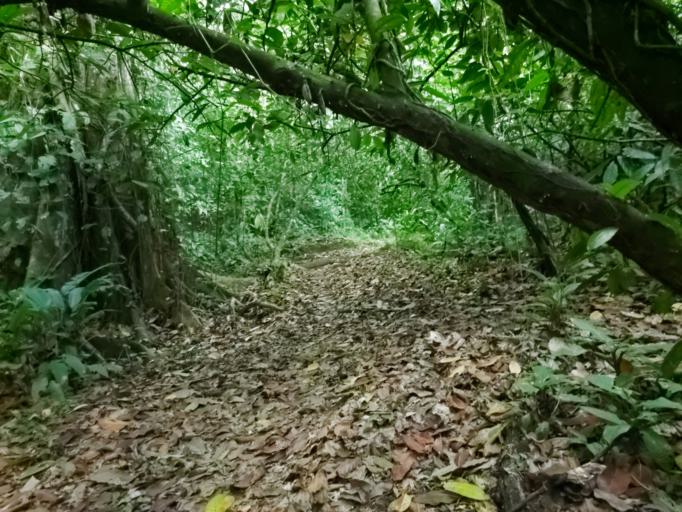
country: PA
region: Bocas del Toro
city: Barranco
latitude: 9.6450
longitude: -82.7872
